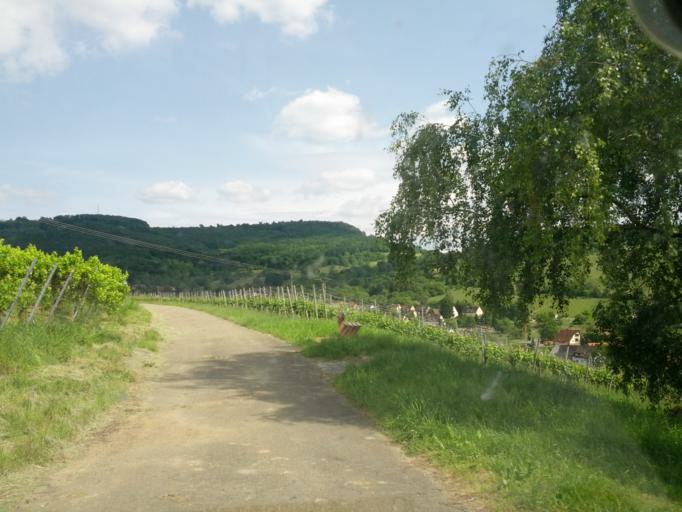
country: DE
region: Baden-Wuerttemberg
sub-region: Freiburg Region
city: Ebringen
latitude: 47.9598
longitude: 7.7751
